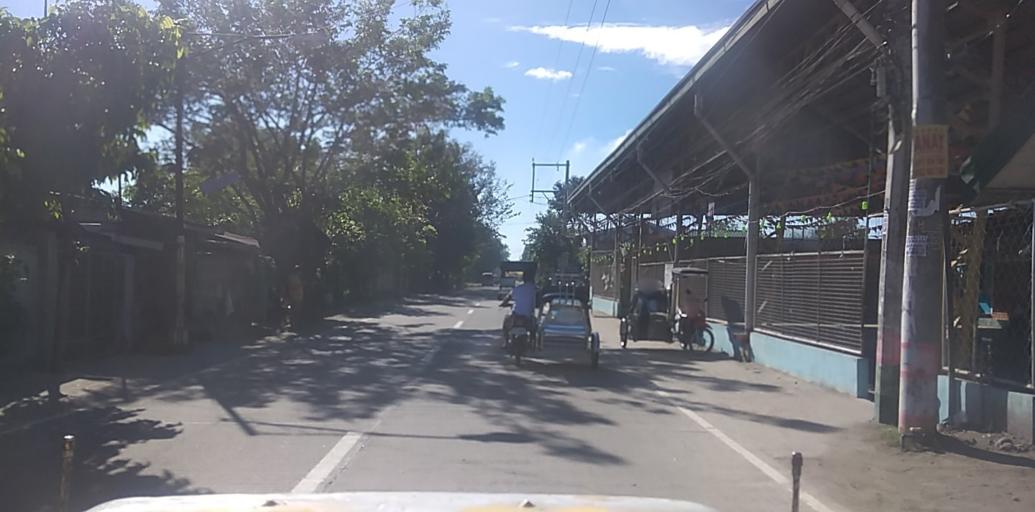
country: PH
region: Central Luzon
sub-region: Province of Pampanga
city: San Patricio
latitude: 15.0852
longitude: 120.7152
